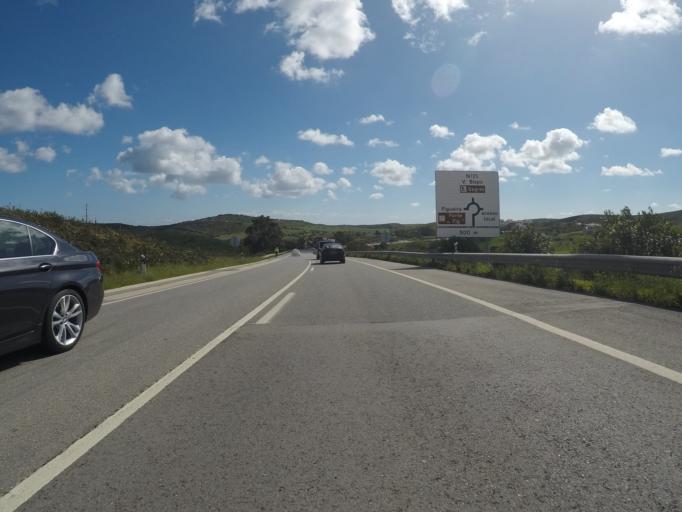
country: PT
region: Faro
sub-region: Vila do Bispo
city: Vila do Bispo
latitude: 37.0772
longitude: -8.8437
